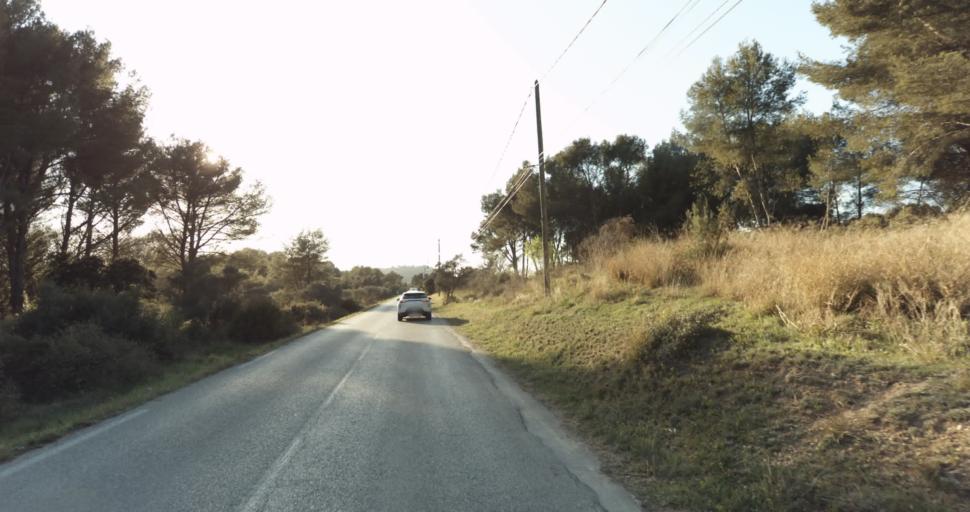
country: FR
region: Provence-Alpes-Cote d'Azur
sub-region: Departement des Bouches-du-Rhone
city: Velaux
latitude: 43.5384
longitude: 5.2731
